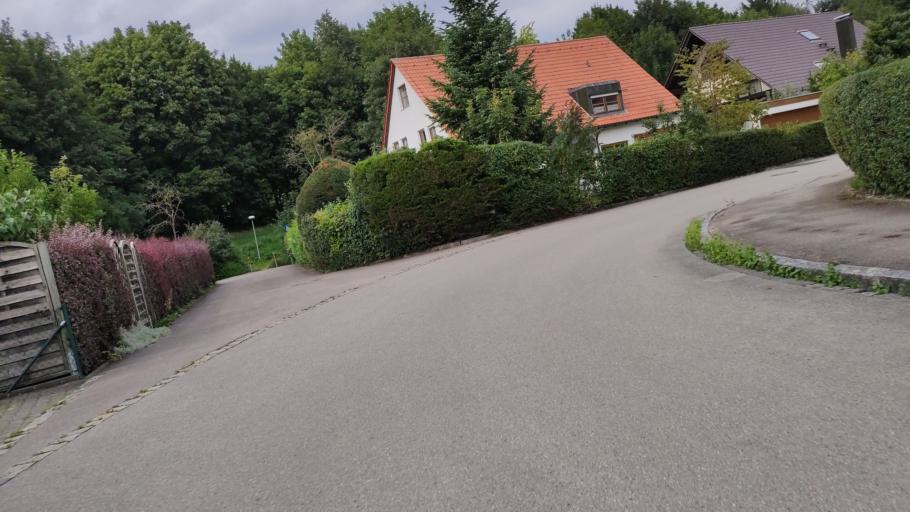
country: DE
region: Bavaria
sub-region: Swabia
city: Konigsbrunn
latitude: 48.2691
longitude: 10.8762
